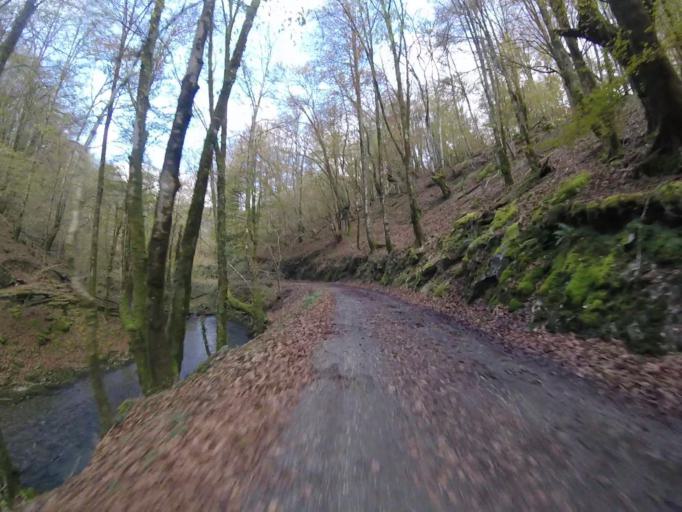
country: ES
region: Navarre
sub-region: Provincia de Navarra
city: Goizueta
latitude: 43.1996
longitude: -1.8049
